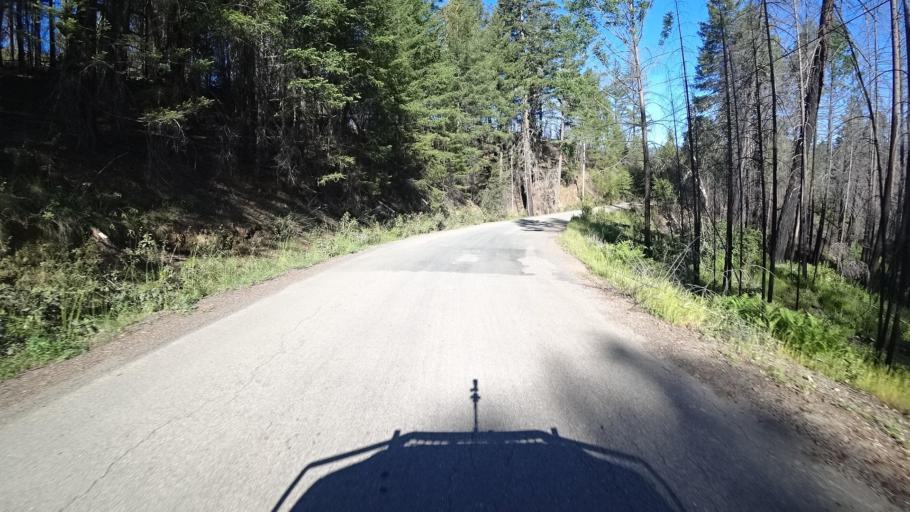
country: US
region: California
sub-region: Lake County
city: Upper Lake
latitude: 39.4024
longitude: -122.9619
